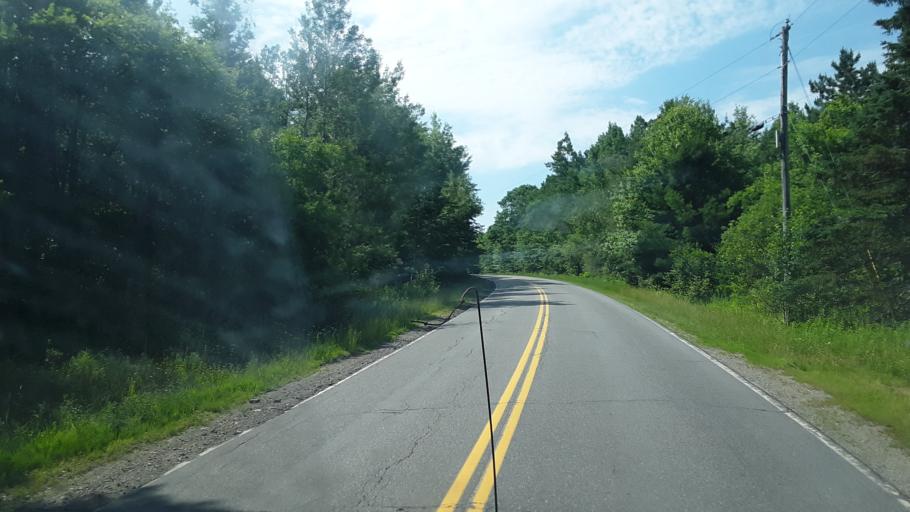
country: US
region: Maine
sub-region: Waldo County
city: Swanville
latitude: 44.5612
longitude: -68.9542
